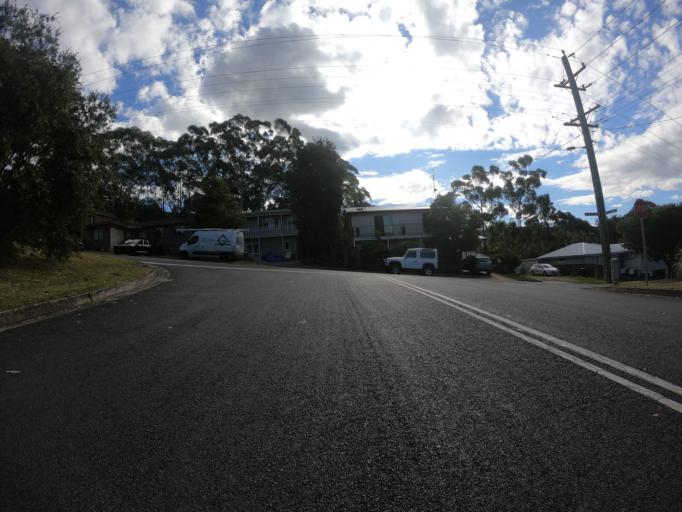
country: AU
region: New South Wales
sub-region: Wollongong
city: Bulli
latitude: -34.3317
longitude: 150.9028
